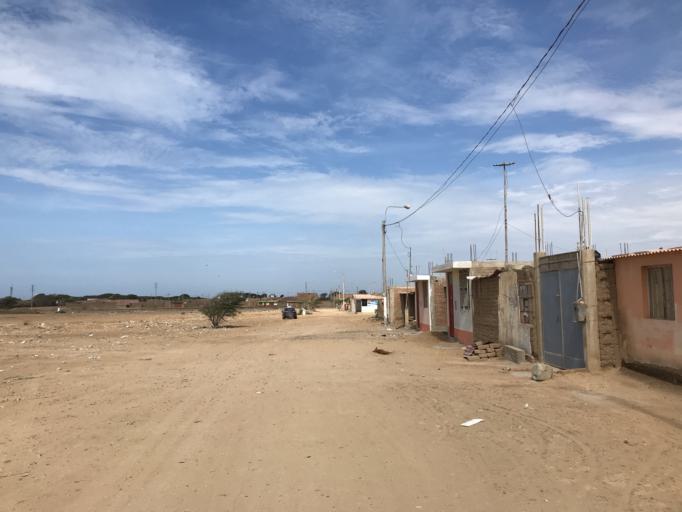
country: PE
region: Lambayeque
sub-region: Provincia de Chiclayo
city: Eten
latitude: -6.8993
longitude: -79.8419
